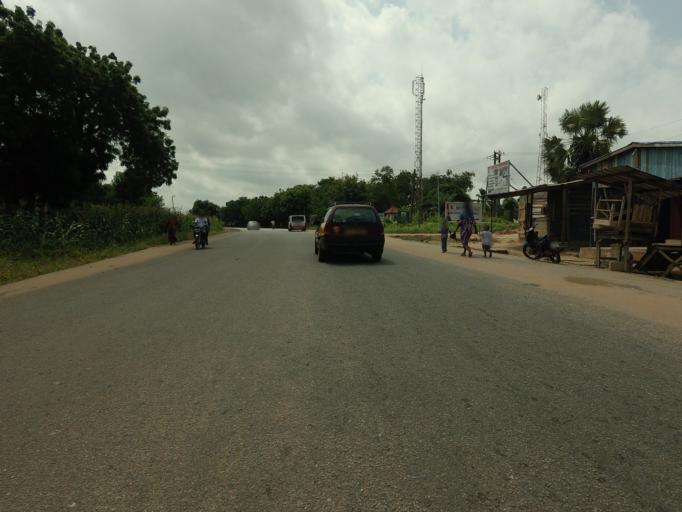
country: TG
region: Maritime
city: Lome
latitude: 6.1173
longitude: 1.1330
